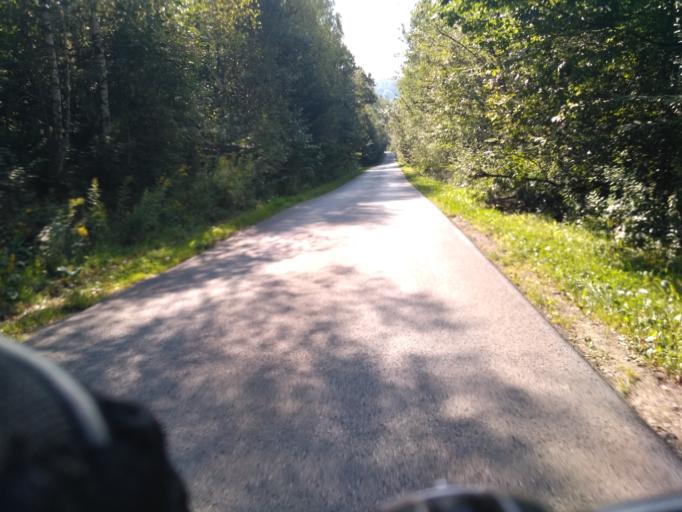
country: PL
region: Subcarpathian Voivodeship
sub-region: Powiat brzozowski
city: Golcowa
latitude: 49.7924
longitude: 22.0203
